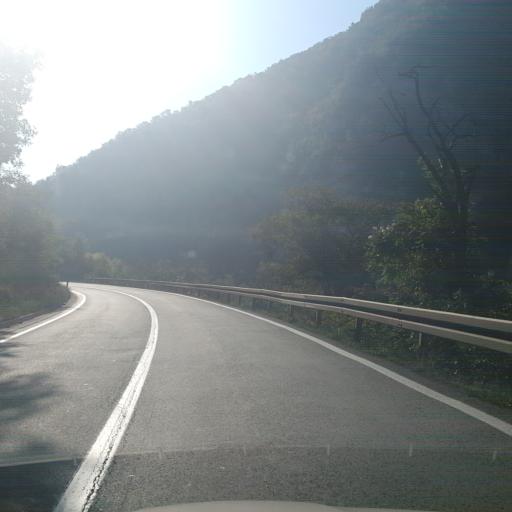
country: RS
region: Central Serbia
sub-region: Nisavski Okrug
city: Svrljig
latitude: 43.3284
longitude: 22.1006
